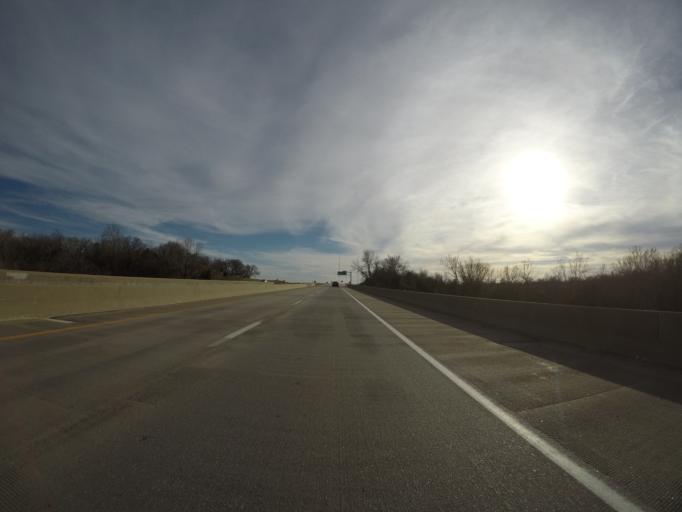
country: US
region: Kansas
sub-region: Franklin County
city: Ottawa
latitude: 38.6001
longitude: -95.2333
